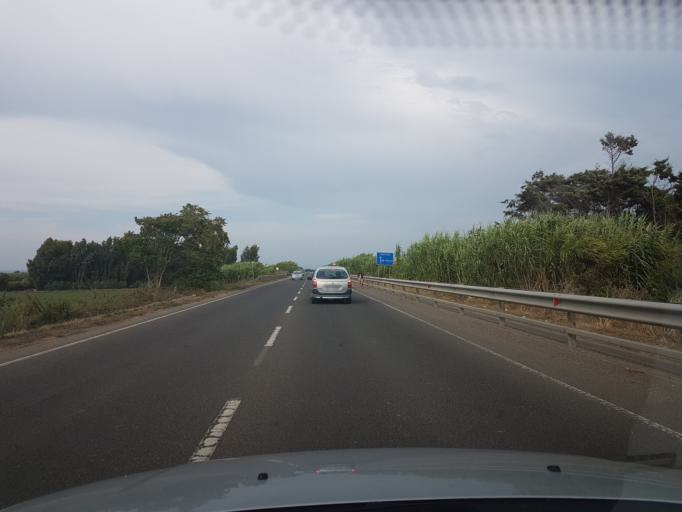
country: IT
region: Sardinia
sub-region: Provincia di Oristano
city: Solanas
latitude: 39.9154
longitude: 8.5461
